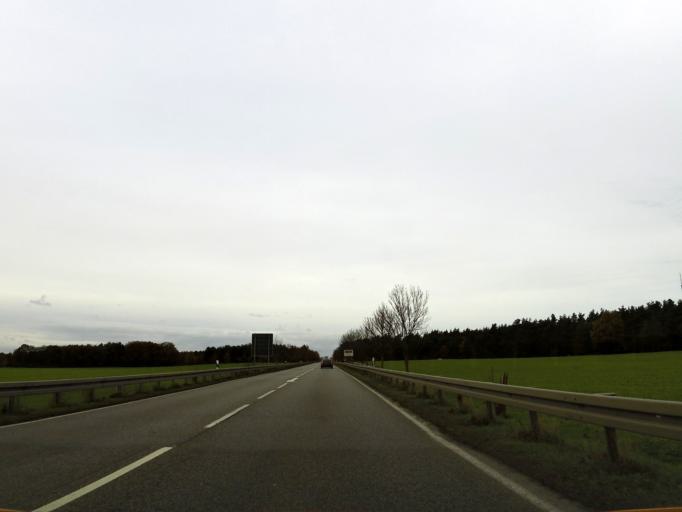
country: DE
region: Saxony-Anhalt
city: Salzwedel
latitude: 52.8276
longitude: 11.1946
